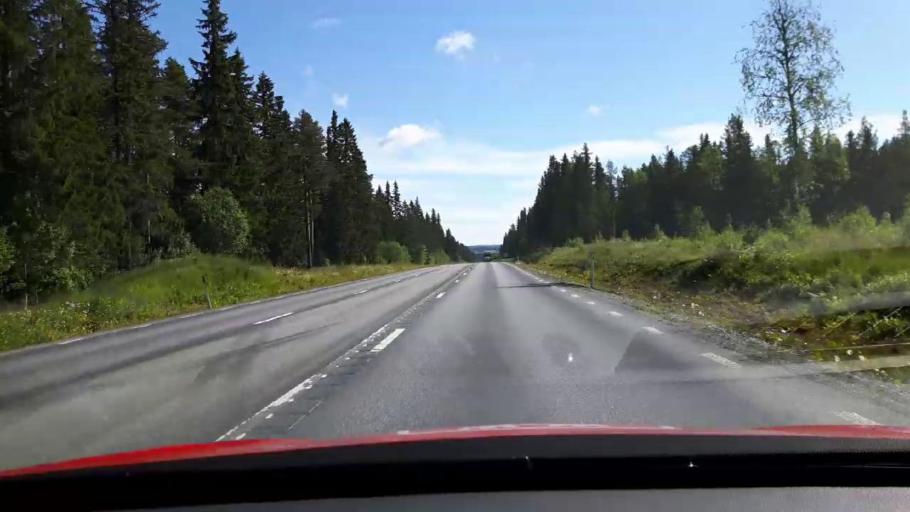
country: SE
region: Jaemtland
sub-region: OEstersunds Kommun
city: Lit
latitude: 63.2493
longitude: 14.8002
